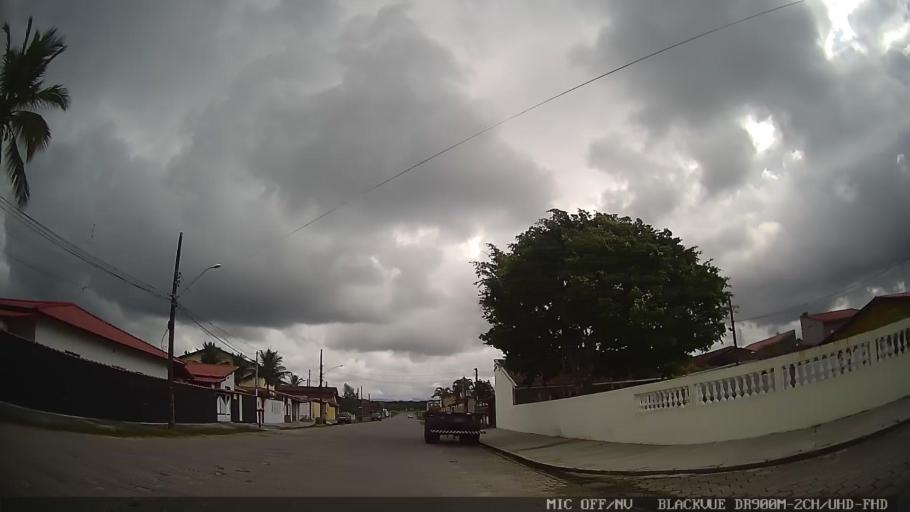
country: BR
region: Sao Paulo
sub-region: Itanhaem
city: Itanhaem
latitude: -24.2030
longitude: -46.8430
